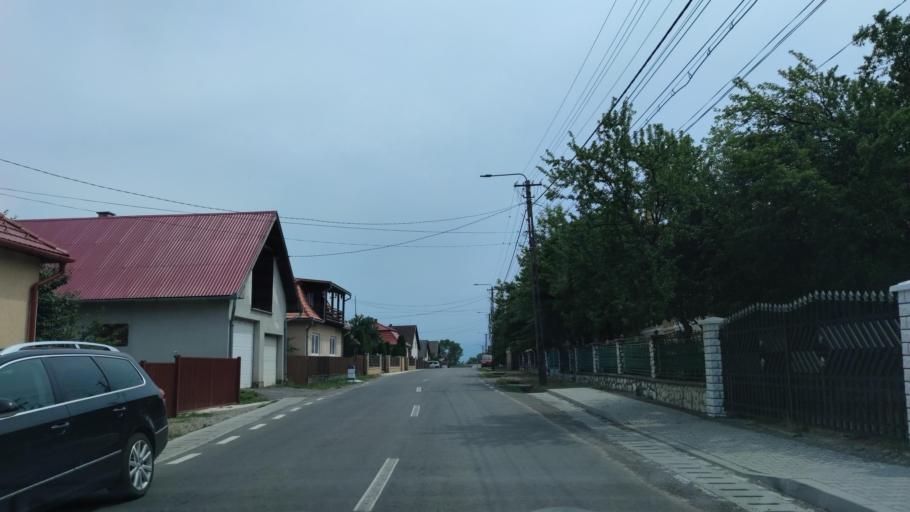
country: RO
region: Harghita
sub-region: Comuna Remetea
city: Remetea
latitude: 46.8076
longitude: 25.4599
